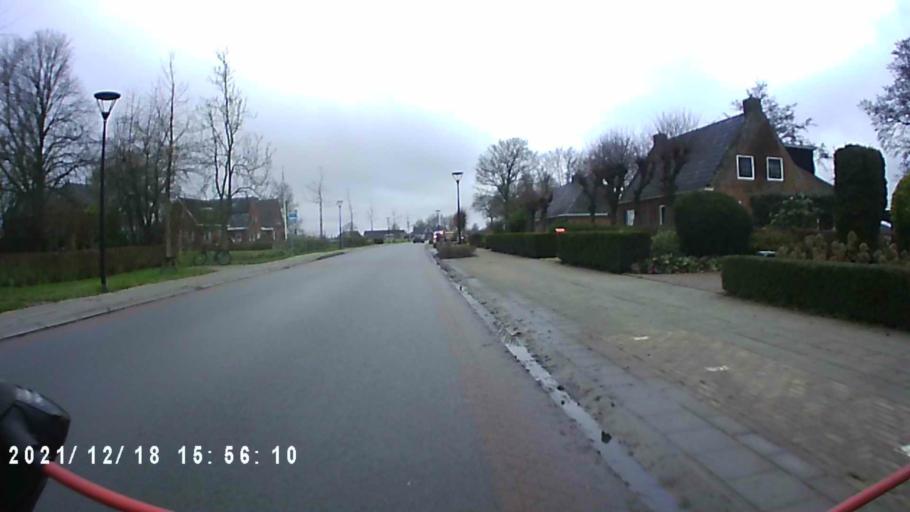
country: NL
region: Friesland
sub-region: Gemeente Dongeradeel
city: Anjum
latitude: 53.3318
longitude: 6.0997
